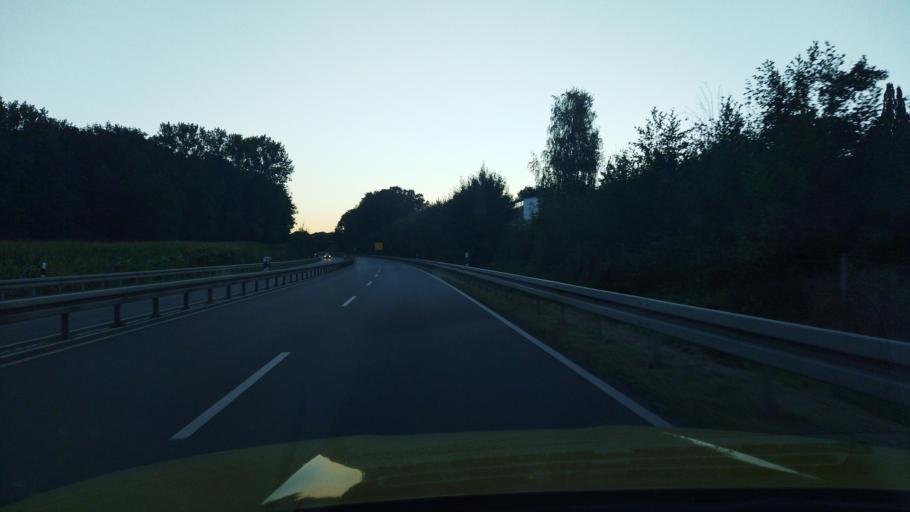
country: DE
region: Lower Saxony
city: Ostercappeln
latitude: 52.3404
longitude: 8.2240
